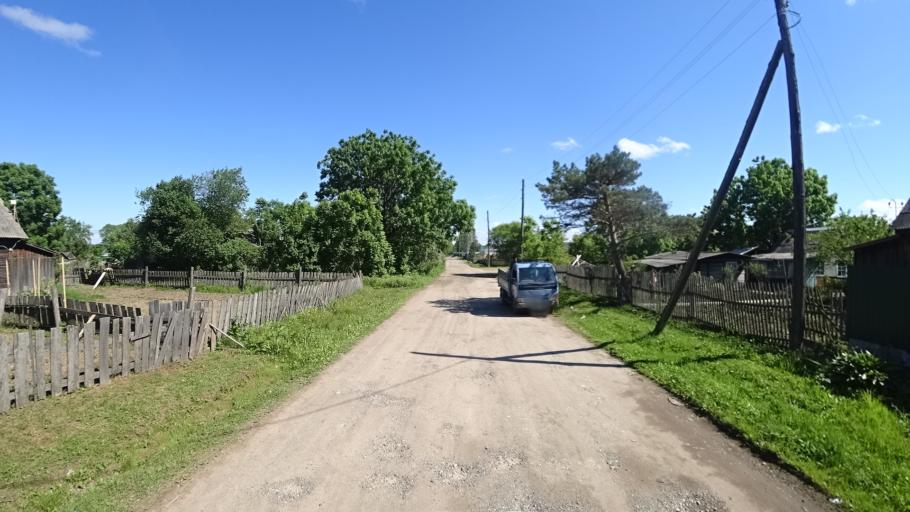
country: RU
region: Khabarovsk Krai
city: Khor
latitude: 47.8869
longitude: 135.0346
